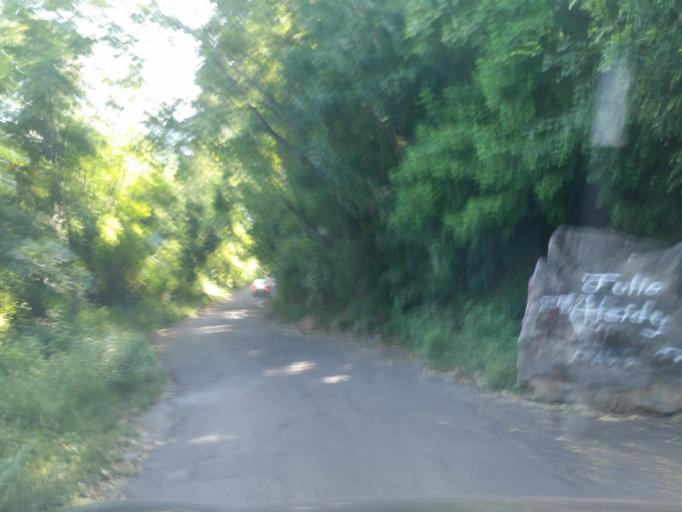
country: NI
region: Masaya
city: Catarina
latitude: 11.9402
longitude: -86.0541
